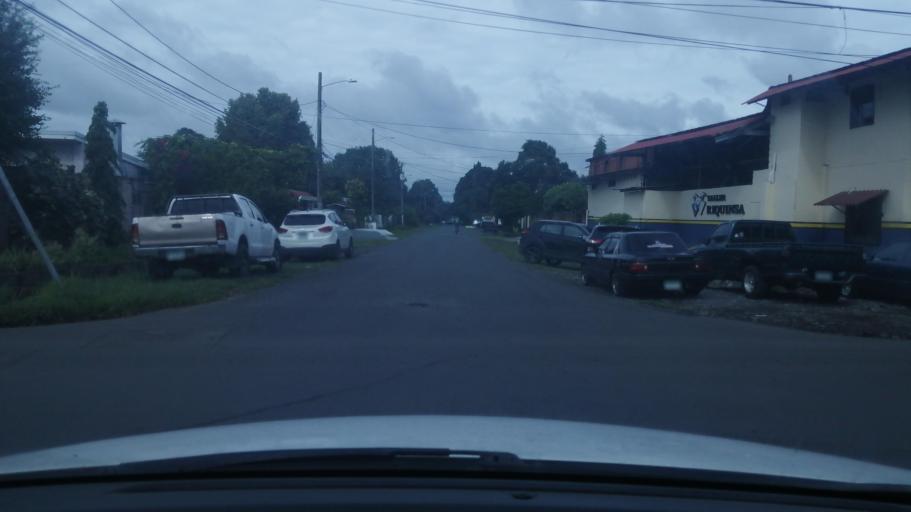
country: PA
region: Chiriqui
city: David
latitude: 8.4362
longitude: -82.4301
